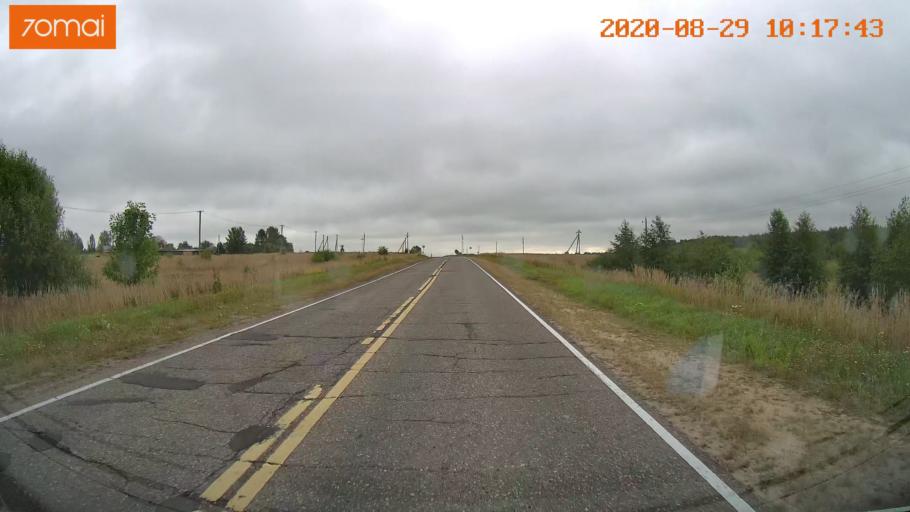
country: RU
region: Ivanovo
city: Yur'yevets
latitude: 57.3333
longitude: 42.8198
